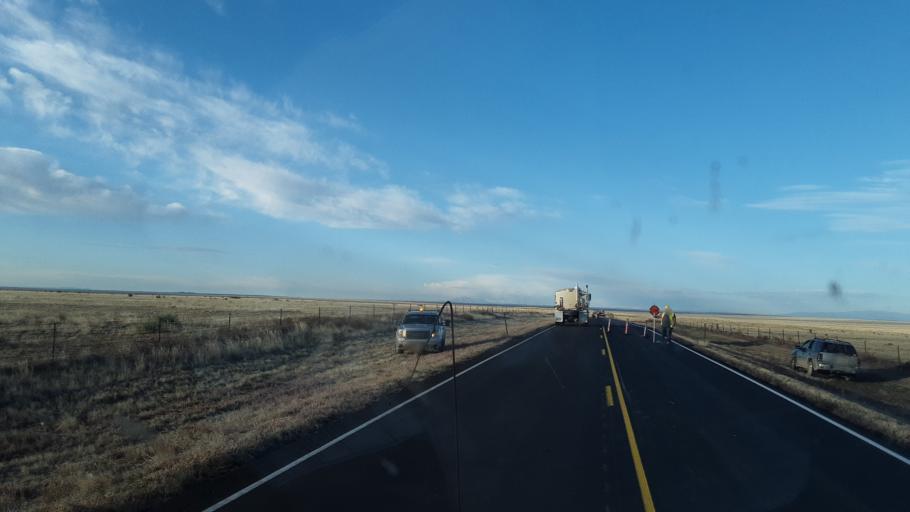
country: US
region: Colorado
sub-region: Otero County
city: Rocky Ford
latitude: 37.9641
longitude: -103.8385
